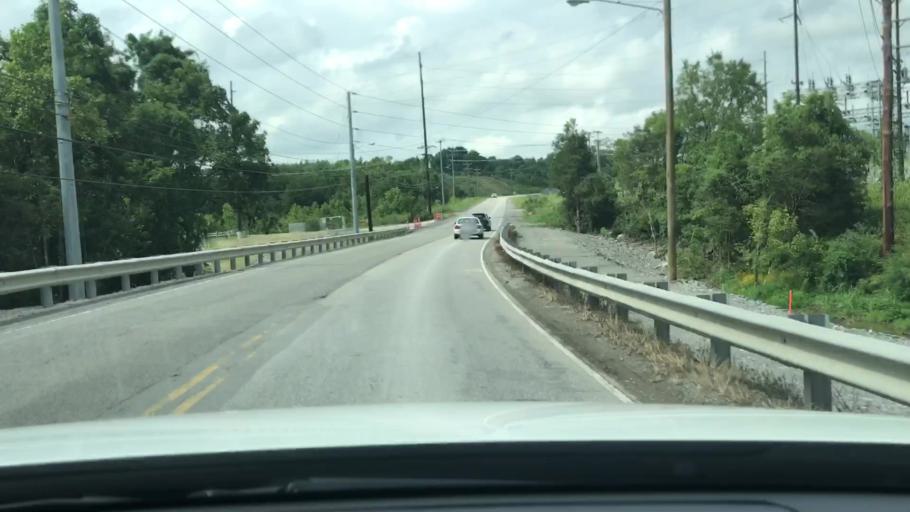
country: US
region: Tennessee
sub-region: Davidson County
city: Oak Hill
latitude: 36.0954
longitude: -86.6906
